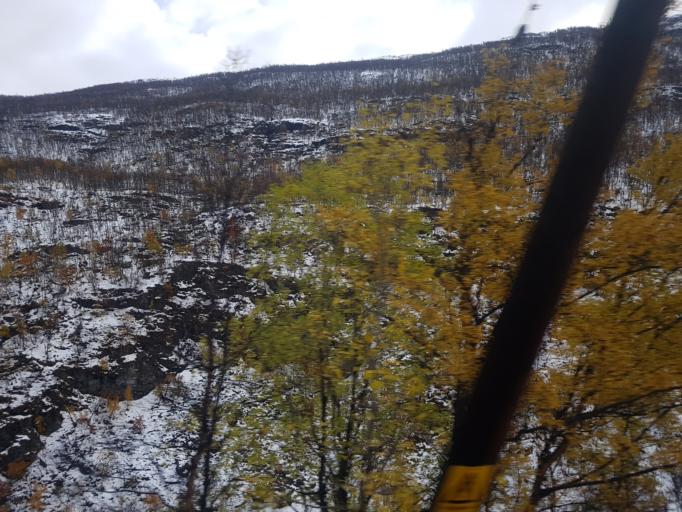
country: NO
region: Sor-Trondelag
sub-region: Oppdal
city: Oppdal
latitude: 62.3568
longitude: 9.6304
